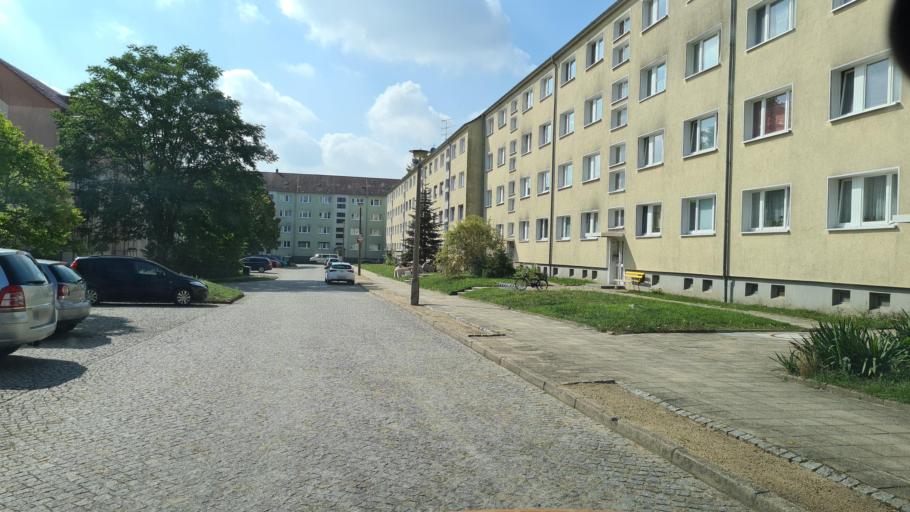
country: DE
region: Brandenburg
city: Luckau
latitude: 51.8500
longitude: 13.6974
